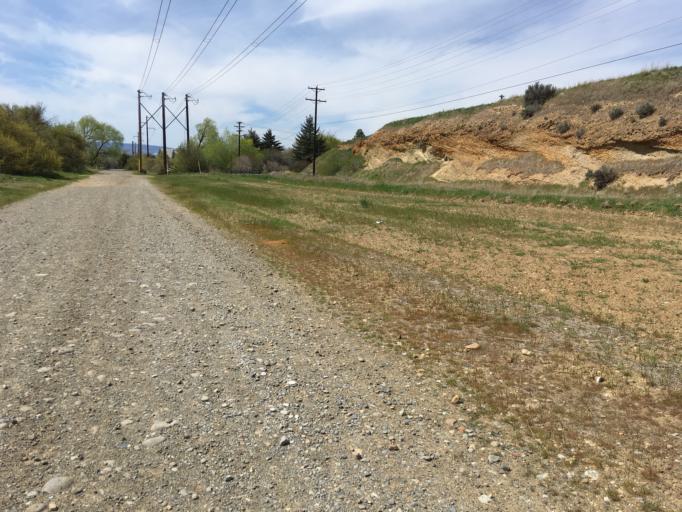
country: US
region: Washington
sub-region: Kittitas County
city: Ellensburg
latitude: 47.0003
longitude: -120.5277
